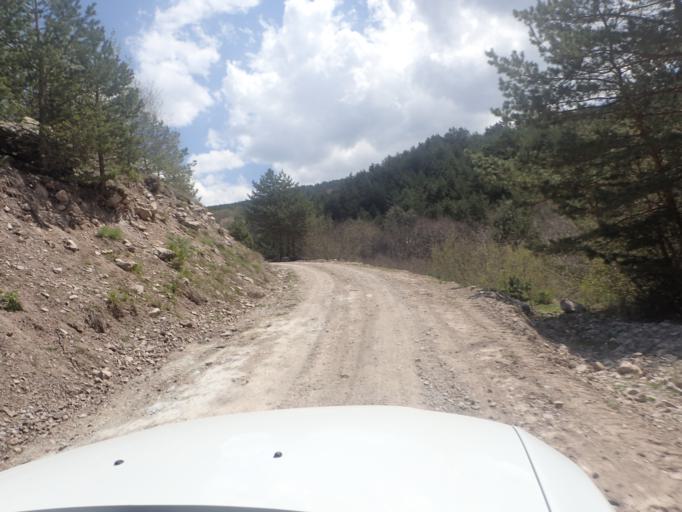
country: TR
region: Ordu
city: Mesudiye
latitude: 40.4161
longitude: 37.8483
